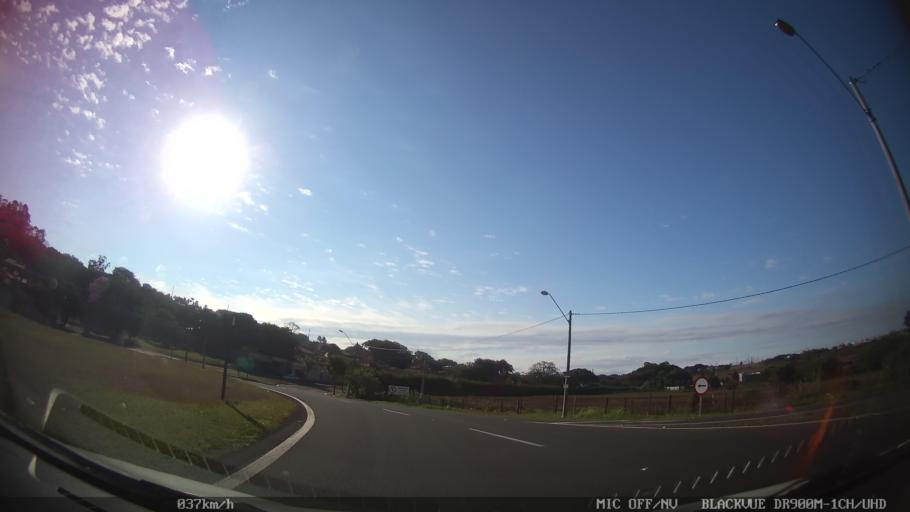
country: BR
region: Sao Paulo
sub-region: Piracicaba
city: Piracicaba
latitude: -22.6911
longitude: -47.6346
